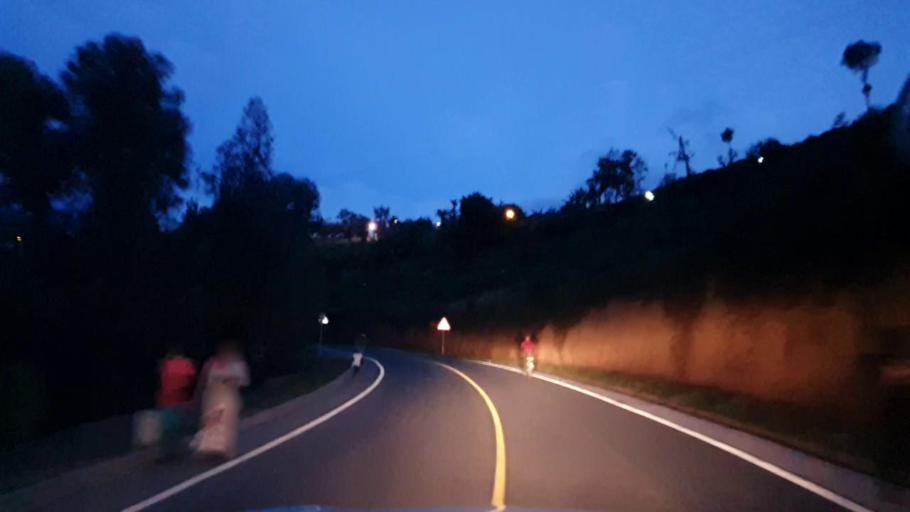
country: RW
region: Southern Province
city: Gikongoro
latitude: -2.4667
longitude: 29.5705
